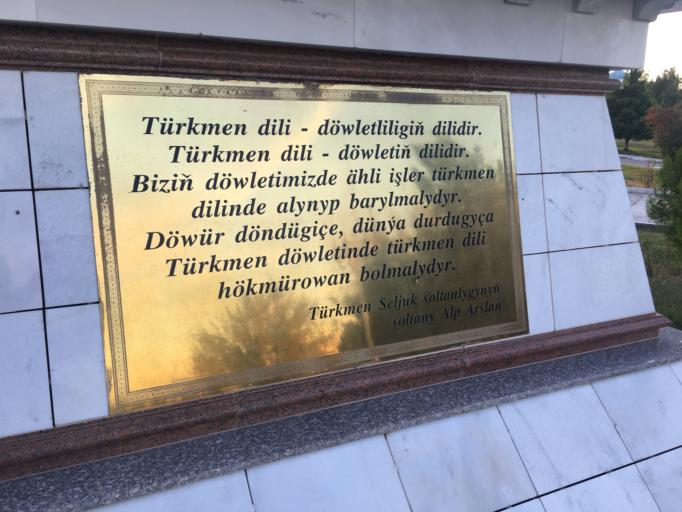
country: TM
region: Ahal
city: Ashgabat
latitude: 37.8861
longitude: 58.3531
